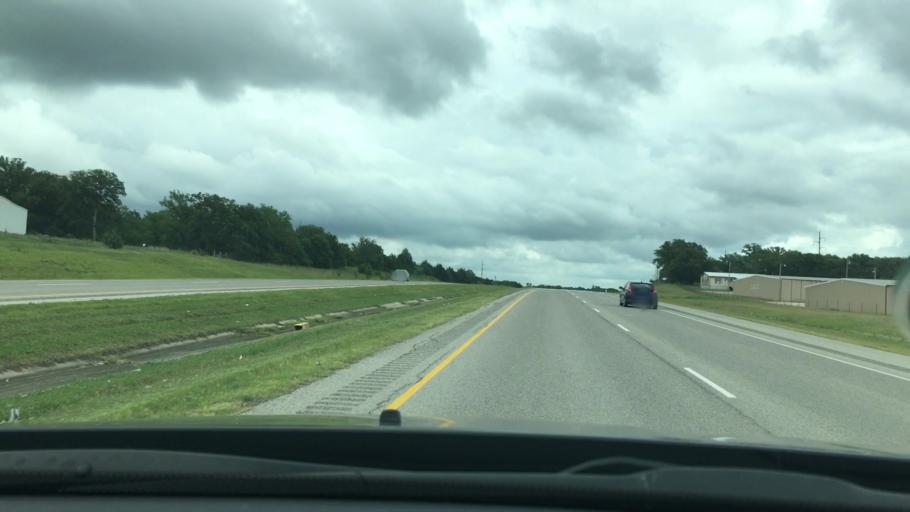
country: US
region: Oklahoma
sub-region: Carter County
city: Ardmore
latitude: 34.1336
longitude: -97.0965
